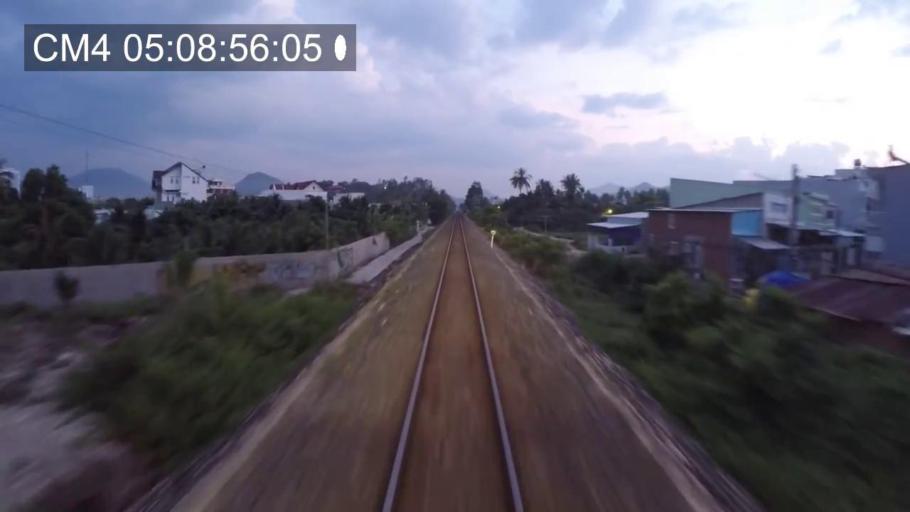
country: VN
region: Khanh Hoa
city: Nha Trang
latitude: 12.2966
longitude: 109.1863
